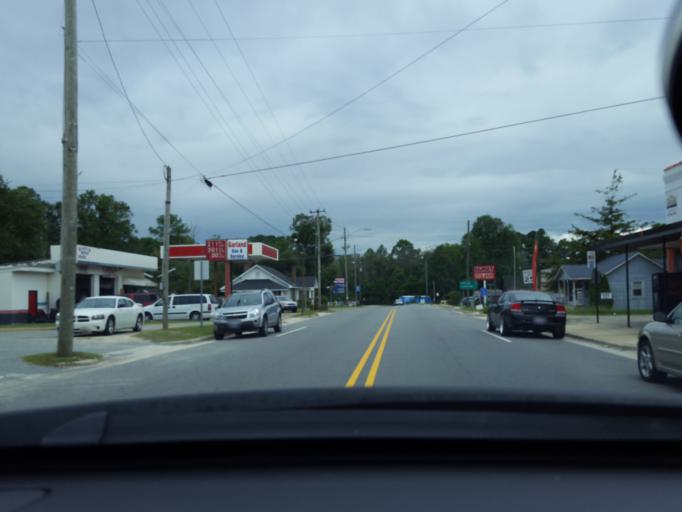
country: US
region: North Carolina
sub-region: Sampson County
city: Roseboro
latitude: 34.7849
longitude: -78.3955
